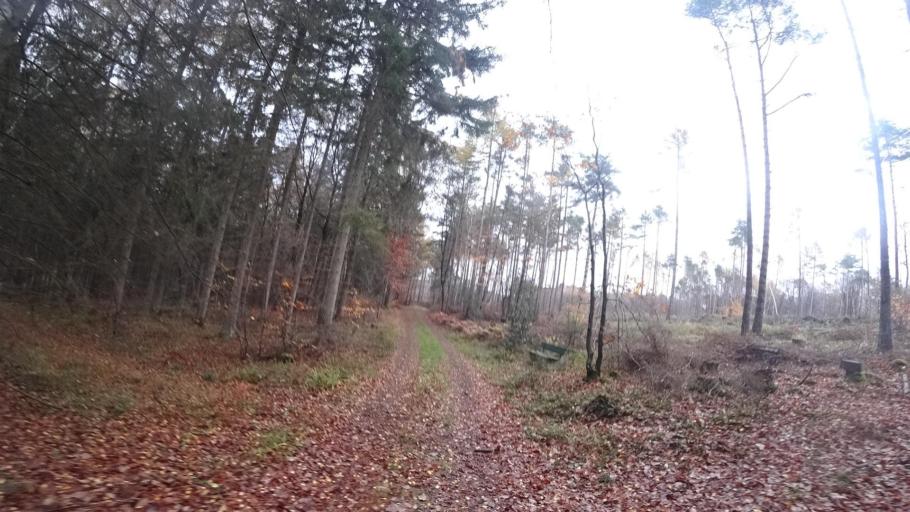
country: DE
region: Rheinland-Pfalz
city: Schalkenbach
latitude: 50.5099
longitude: 7.1293
